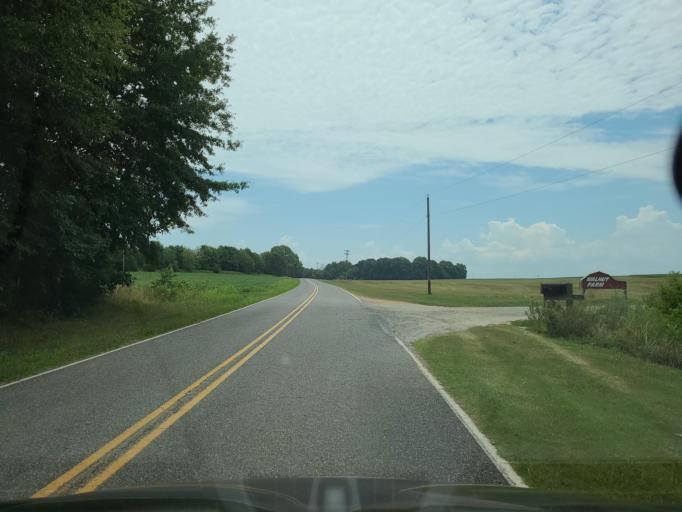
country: US
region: North Carolina
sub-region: Cleveland County
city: Boiling Springs
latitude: 35.2641
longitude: -81.6056
